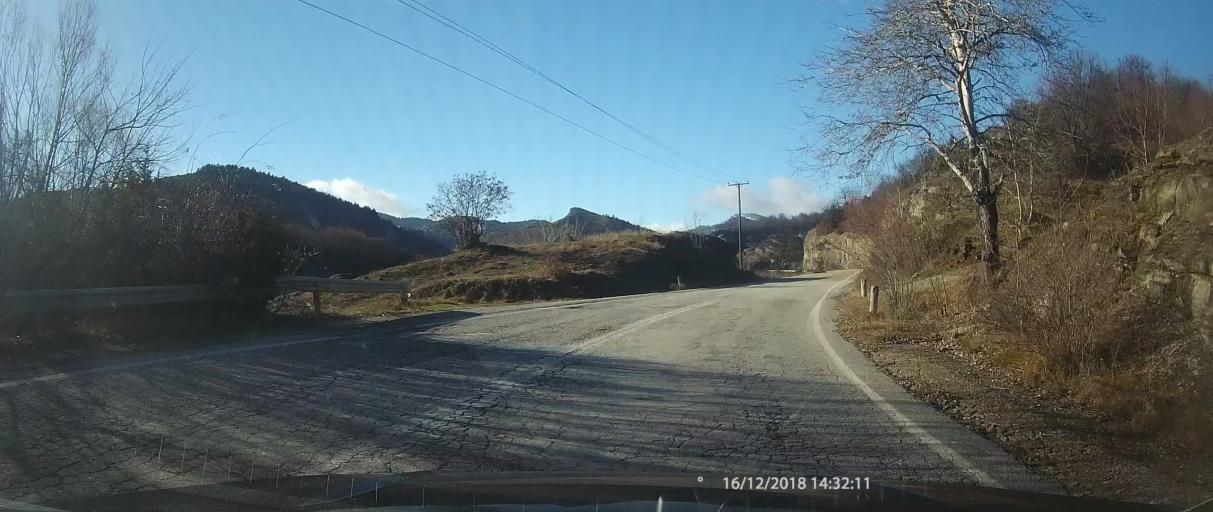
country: GR
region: West Macedonia
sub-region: Nomos Kozanis
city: Tsotili
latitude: 40.1948
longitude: 21.1727
